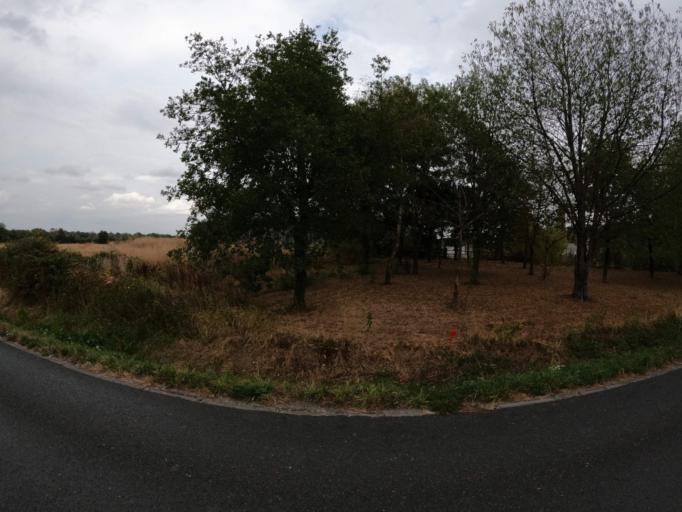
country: FR
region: Pays de la Loire
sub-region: Departement de Maine-et-Loire
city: La Romagne
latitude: 47.0457
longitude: -1.0358
